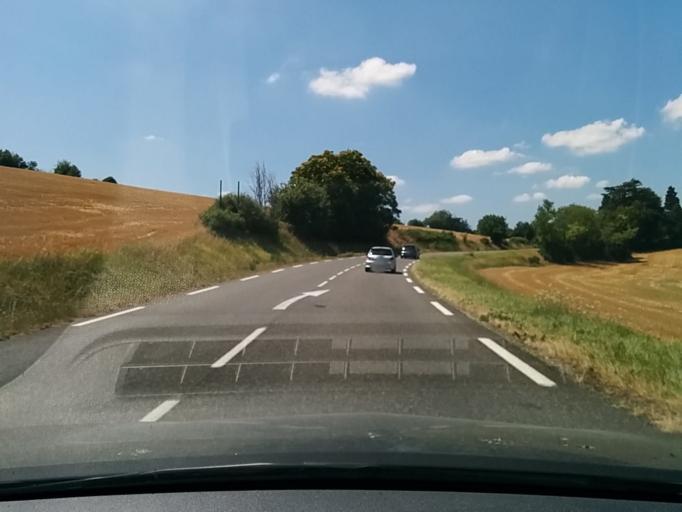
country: FR
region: Midi-Pyrenees
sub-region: Departement du Gers
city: Vic-Fezensac
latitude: 43.7468
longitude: 0.3416
